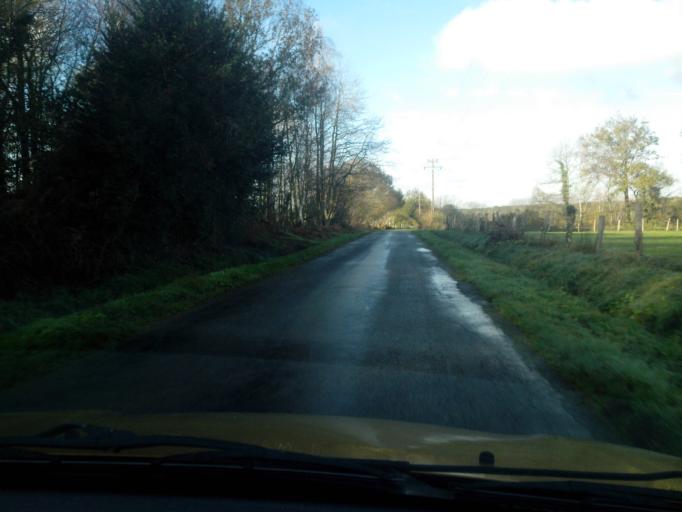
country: FR
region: Brittany
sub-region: Departement du Morbihan
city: Molac
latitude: 47.7296
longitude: -2.4084
